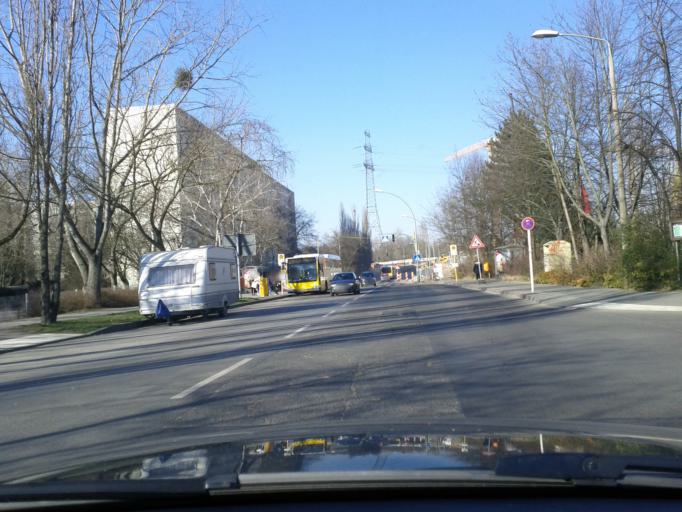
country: DE
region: Berlin
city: Biesdorf
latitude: 52.5108
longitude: 13.5325
